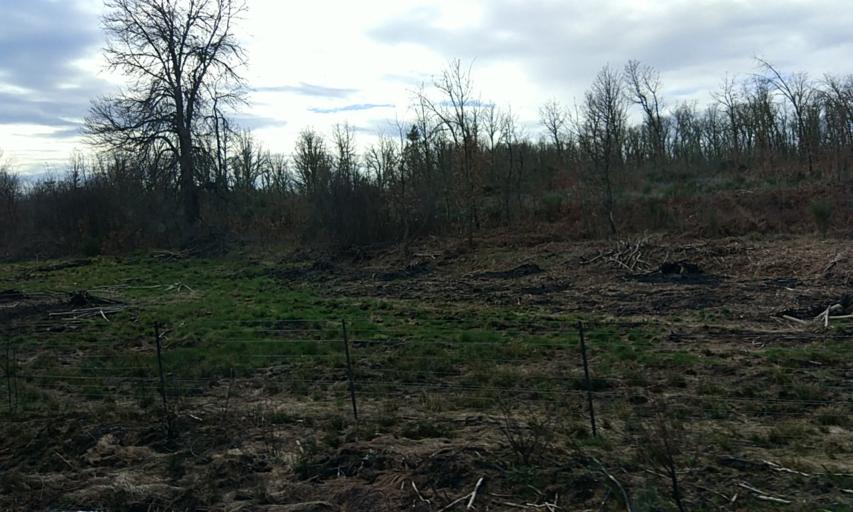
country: ES
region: Castille and Leon
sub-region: Provincia de Salamanca
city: Penaparda
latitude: 40.2971
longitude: -6.6595
